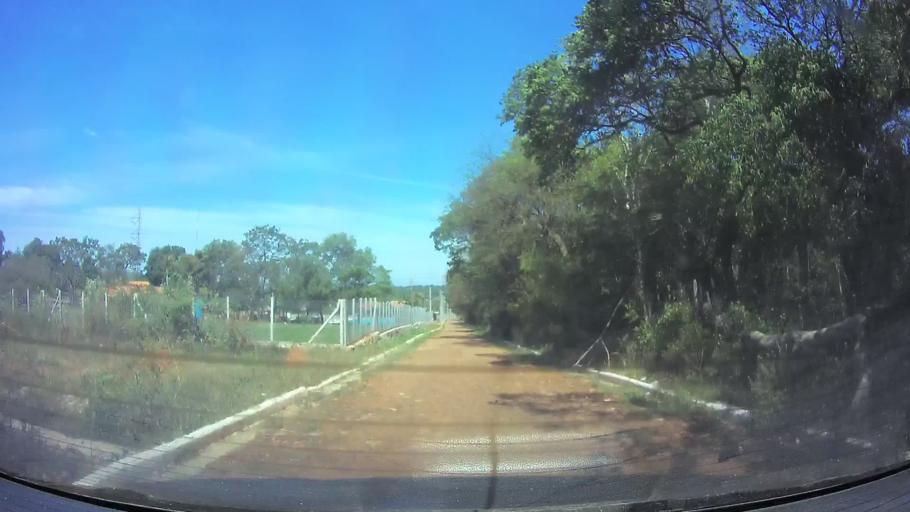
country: PY
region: Central
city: Limpio
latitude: -25.2315
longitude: -57.4372
